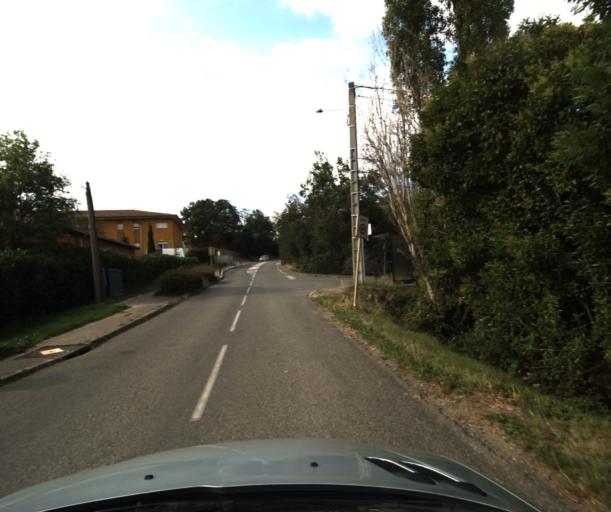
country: FR
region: Midi-Pyrenees
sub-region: Departement de la Haute-Garonne
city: Fonsorbes
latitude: 43.5303
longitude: 1.2310
